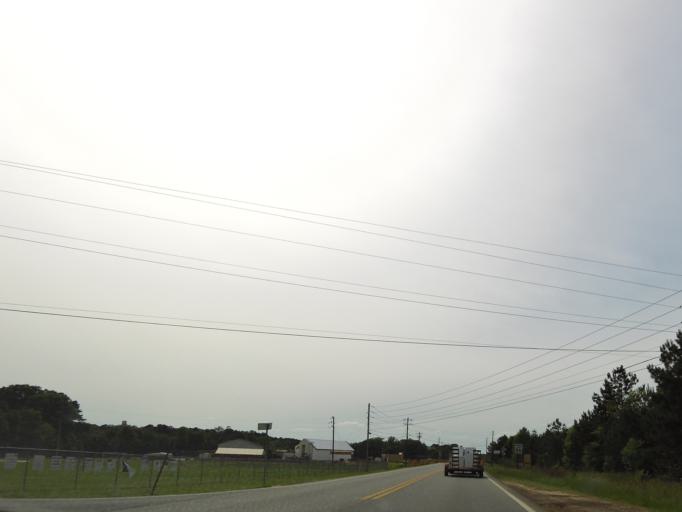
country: US
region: Georgia
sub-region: Houston County
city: Robins Air Force Base
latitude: 32.5491
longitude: -83.6002
